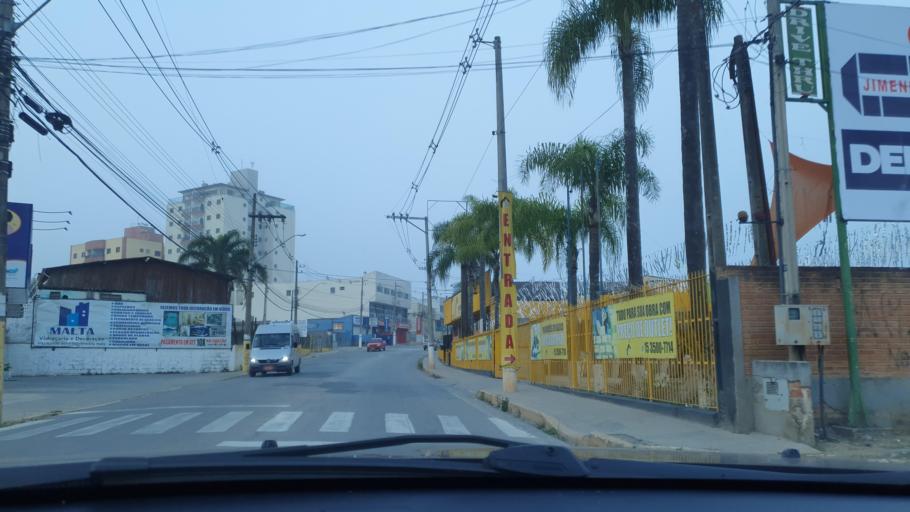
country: BR
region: Sao Paulo
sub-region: Ibiuna
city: Ibiuna
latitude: -23.6582
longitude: -47.2248
